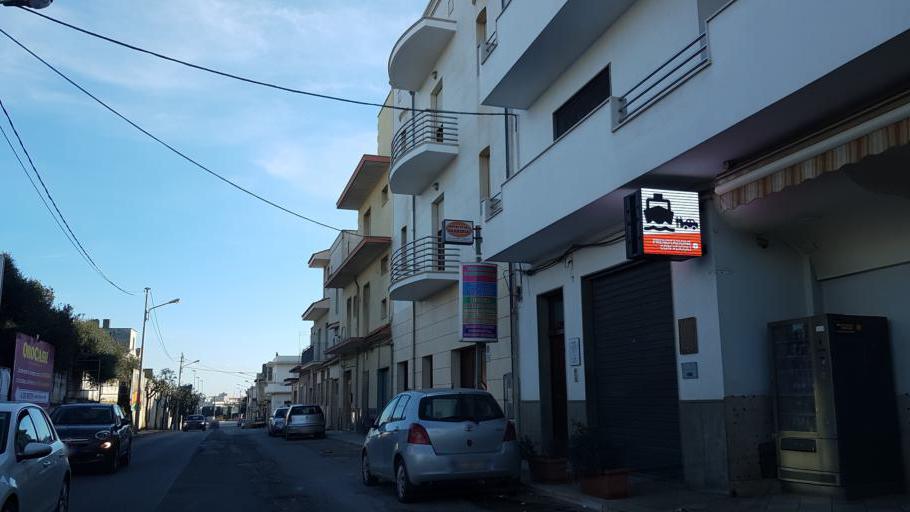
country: IT
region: Apulia
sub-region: Provincia di Brindisi
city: Carovigno
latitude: 40.7081
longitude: 17.6627
